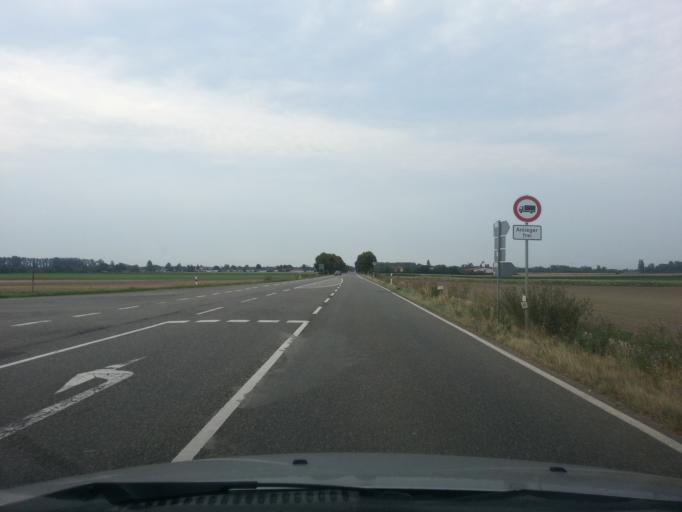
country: DE
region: Rheinland-Pfalz
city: Bobenheim-Roxheim
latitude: 49.6043
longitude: 8.3580
